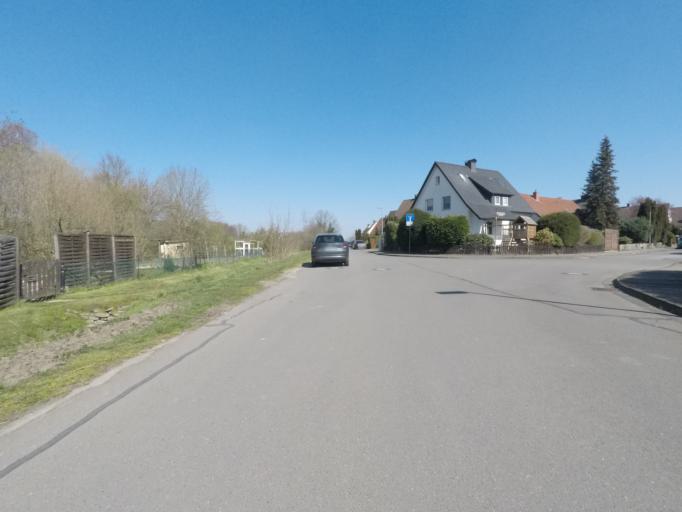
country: DE
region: North Rhine-Westphalia
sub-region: Regierungsbezirk Detmold
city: Herford
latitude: 52.0636
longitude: 8.6163
